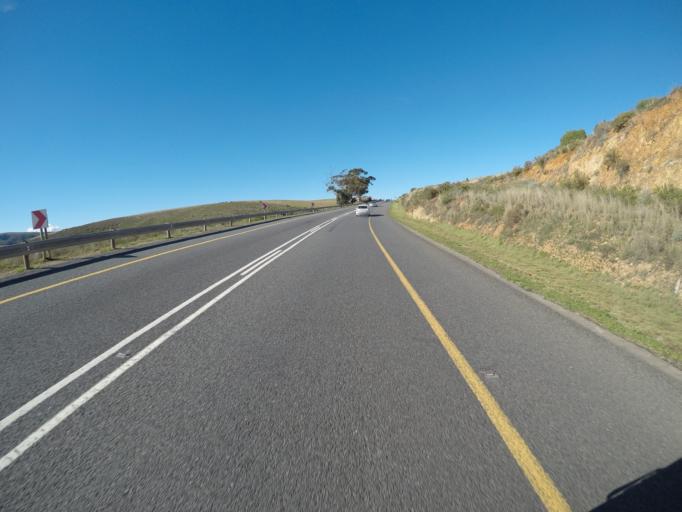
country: ZA
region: Western Cape
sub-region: Overberg District Municipality
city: Caledon
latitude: -34.2319
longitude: 19.2405
